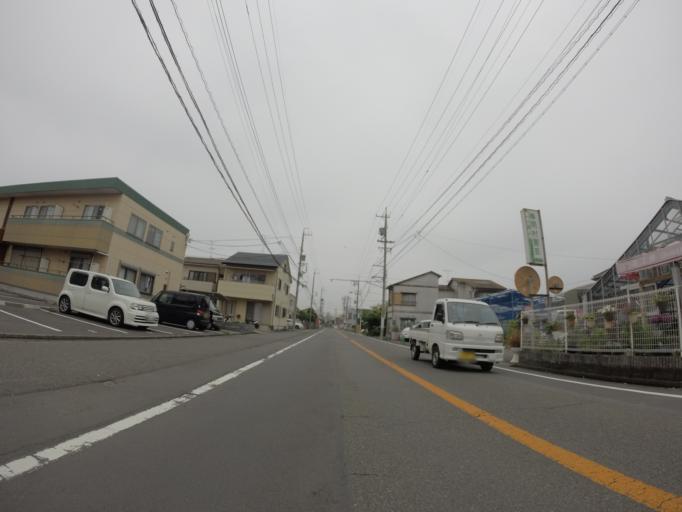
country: JP
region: Shizuoka
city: Shizuoka-shi
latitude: 34.9574
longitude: 138.3910
